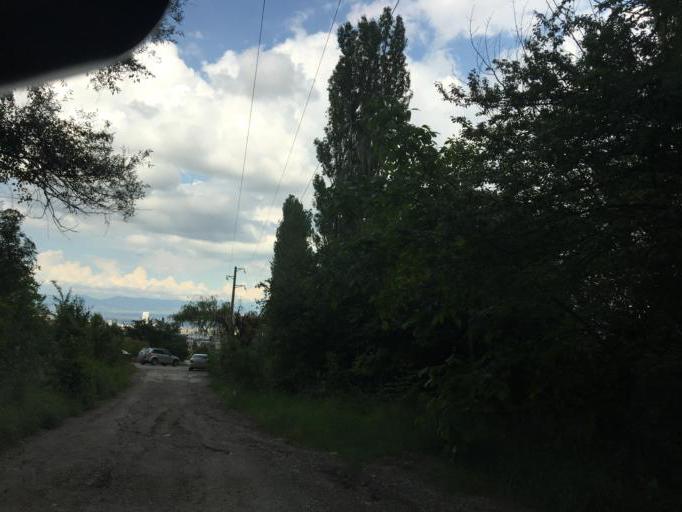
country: BG
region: Sofia-Capital
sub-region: Stolichna Obshtina
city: Sofia
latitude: 42.6122
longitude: 23.3627
